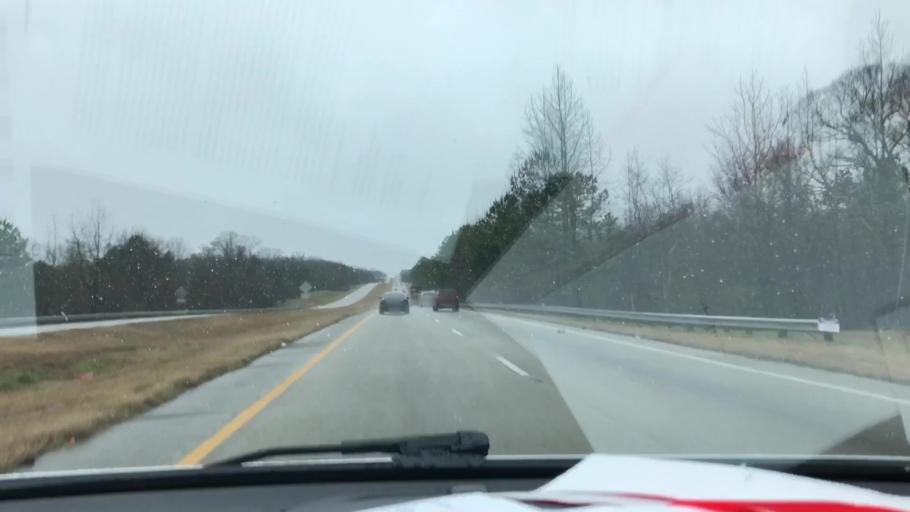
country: US
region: Georgia
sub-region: Gwinnett County
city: Dacula
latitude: 33.9729
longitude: -83.8677
